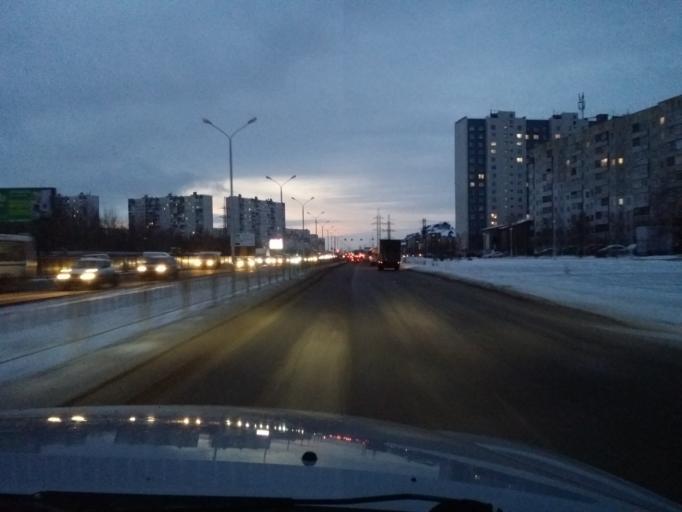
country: RU
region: Khanty-Mansiyskiy Avtonomnyy Okrug
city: Nizhnevartovsk
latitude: 60.9528
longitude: 76.5811
